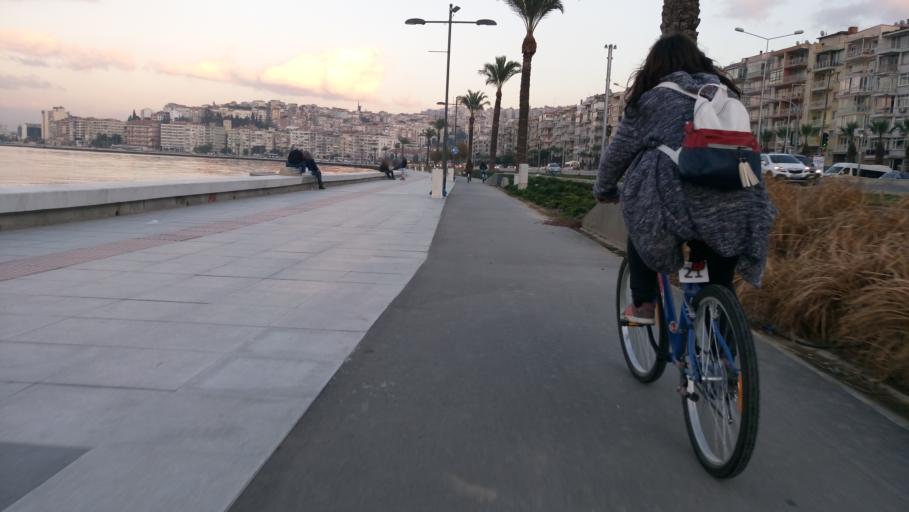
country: TR
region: Izmir
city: Izmir
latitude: 38.4100
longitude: 27.1138
